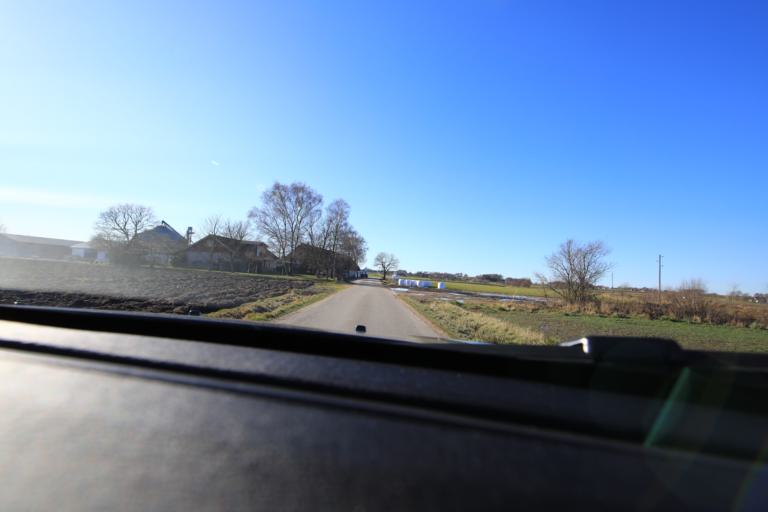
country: SE
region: Halland
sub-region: Varbergs Kommun
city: Tvaaker
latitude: 57.0633
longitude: 12.4132
